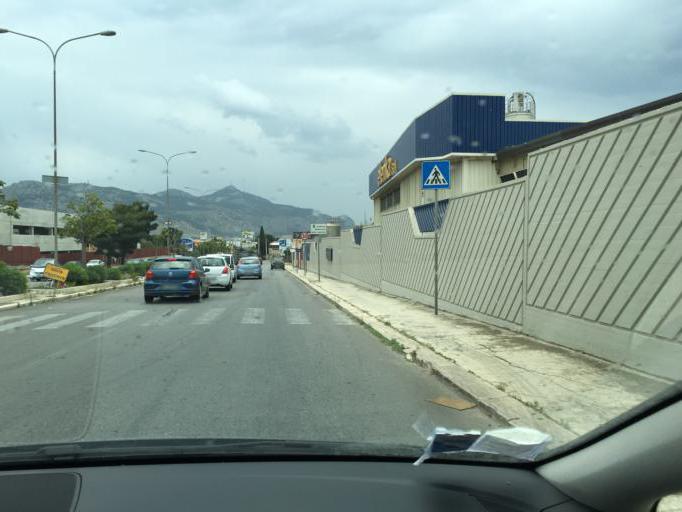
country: IT
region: Sicily
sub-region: Palermo
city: Isola delle Femmine
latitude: 38.1897
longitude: 13.2936
